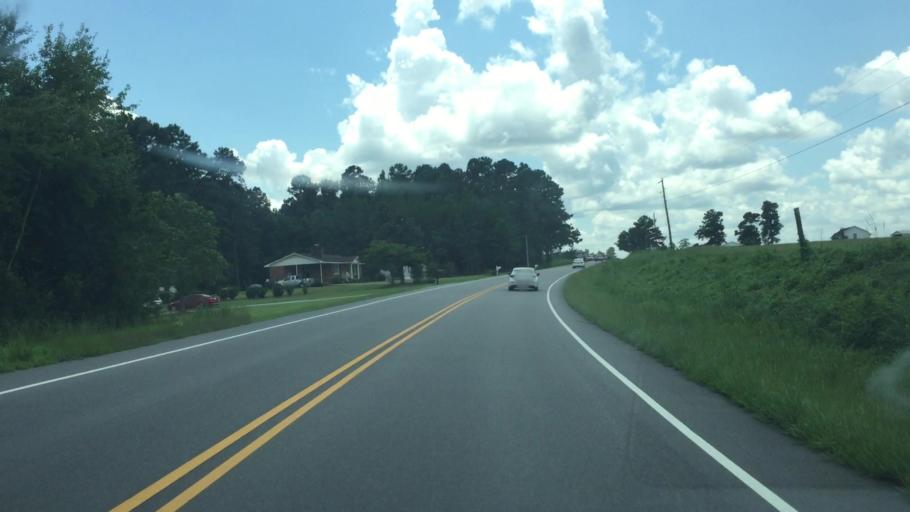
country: US
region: North Carolina
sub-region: Columbus County
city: Tabor City
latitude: 34.2079
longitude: -78.8265
